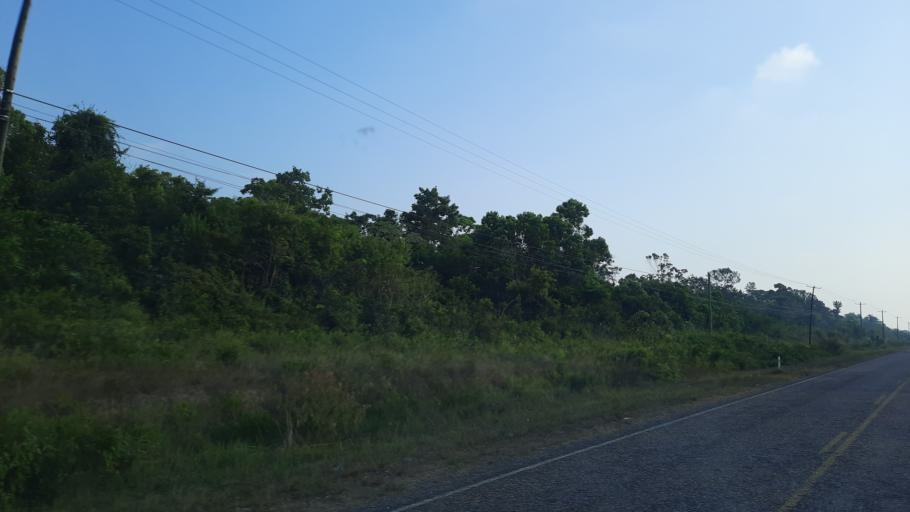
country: BZ
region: Stann Creek
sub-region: Dangriga
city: Dangriga
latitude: 16.9598
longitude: -88.3139
